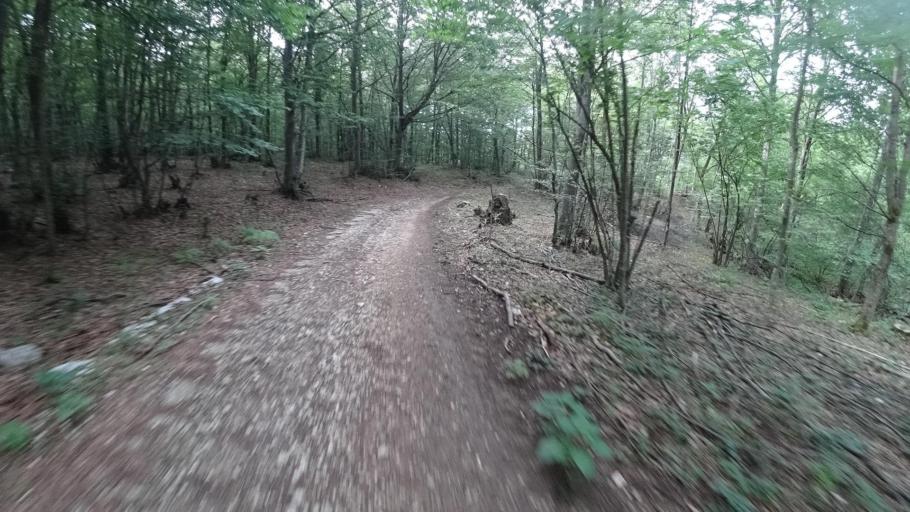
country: HR
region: Licko-Senjska
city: Jezerce
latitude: 44.8996
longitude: 15.6580
